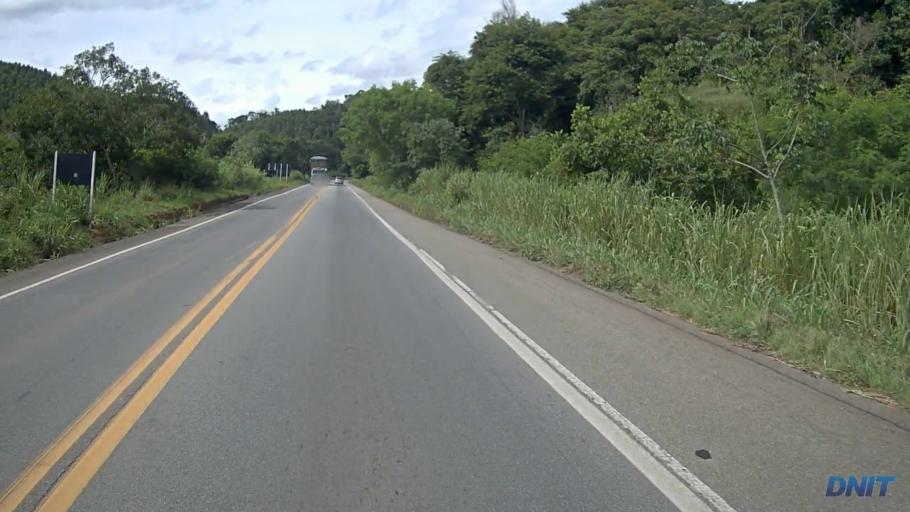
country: BR
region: Minas Gerais
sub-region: Ipaba
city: Ipaba
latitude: -19.3289
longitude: -42.4200
